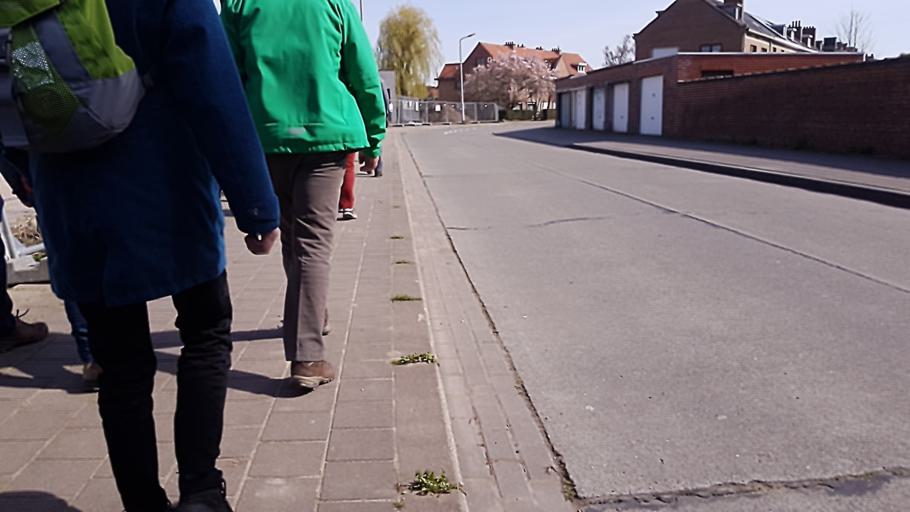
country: BE
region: Flanders
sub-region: Provincie West-Vlaanderen
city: Kortrijk
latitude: 50.8184
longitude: 3.2720
